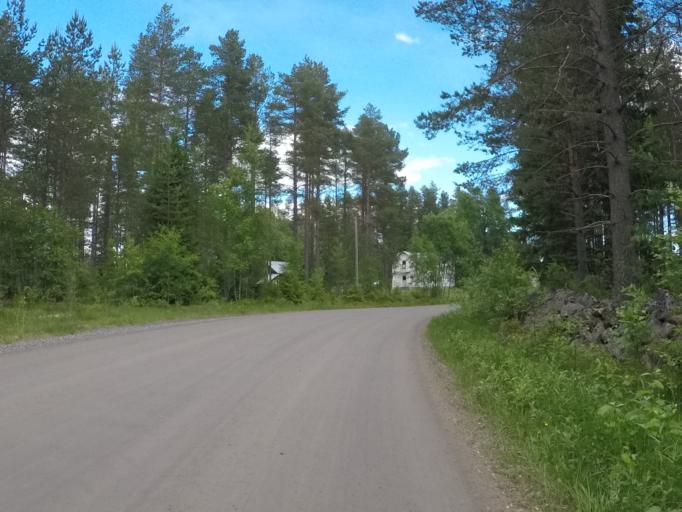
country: SE
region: Vaesterbotten
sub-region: Robertsfors Kommun
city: Robertsfors
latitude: 64.1593
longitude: 20.9196
